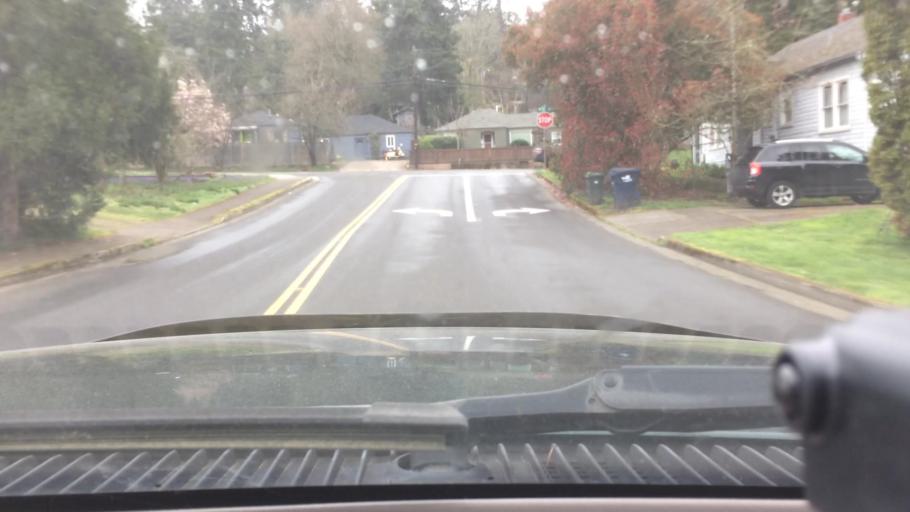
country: US
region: Oregon
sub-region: Lane County
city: Eugene
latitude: 44.0278
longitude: -123.1013
